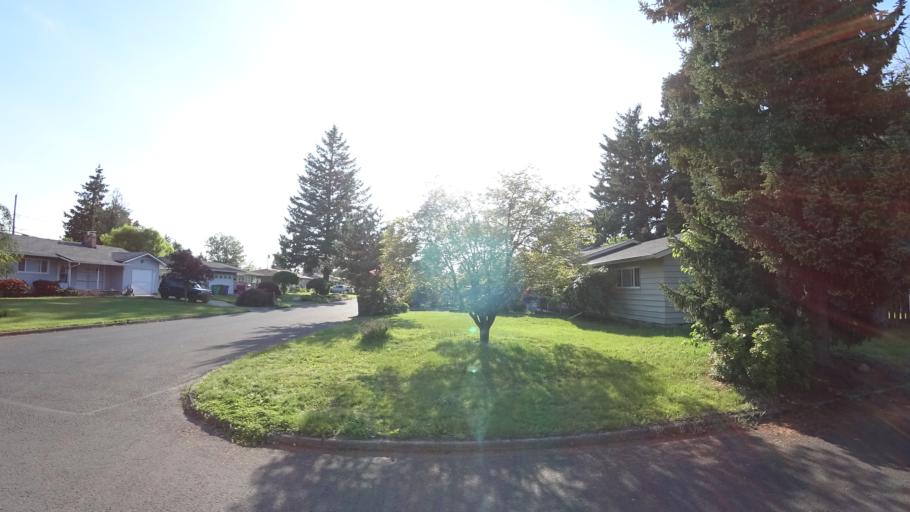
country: US
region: Oregon
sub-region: Multnomah County
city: Fairview
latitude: 45.5159
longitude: -122.4938
